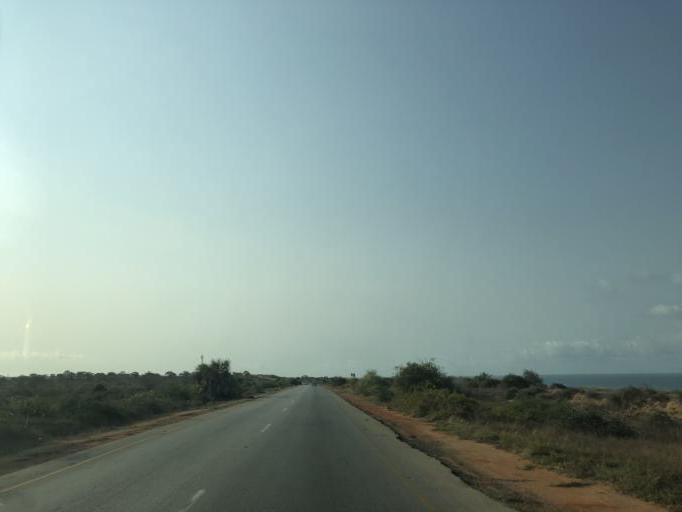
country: AO
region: Luanda
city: Luanda
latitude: -9.1533
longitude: 13.0450
